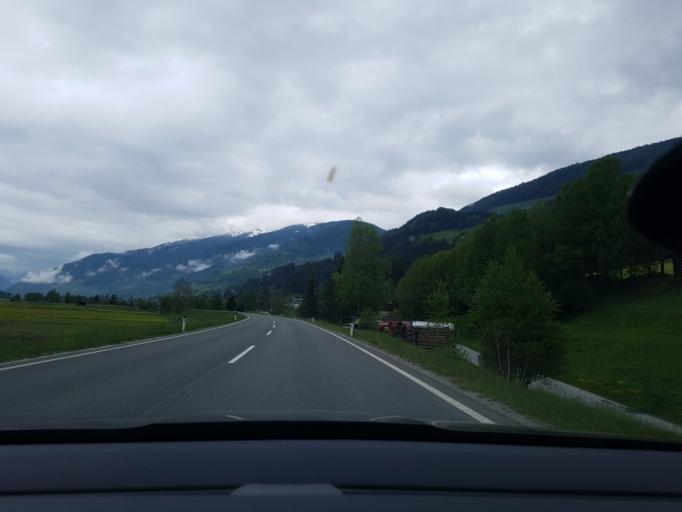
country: AT
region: Salzburg
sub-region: Politischer Bezirk Zell am See
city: Hollersbach im Pinzgau
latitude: 47.2820
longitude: 12.4039
